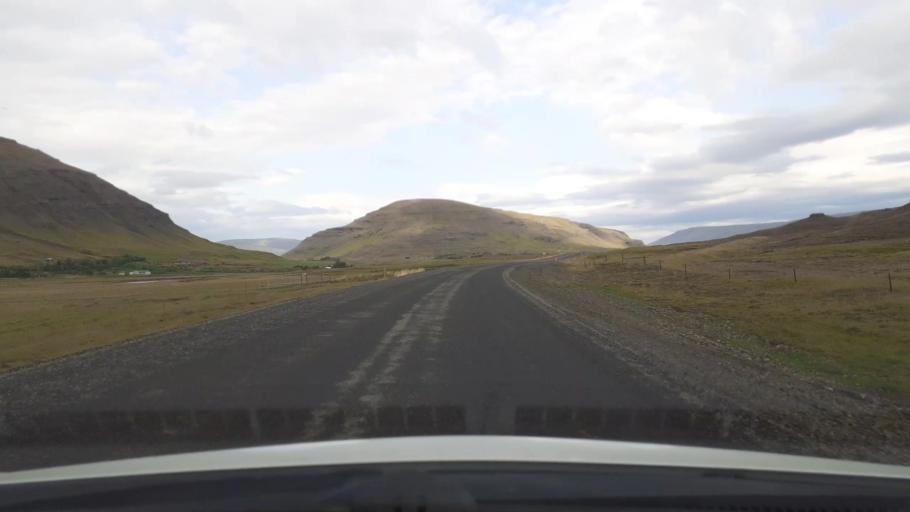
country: IS
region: Capital Region
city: Mosfellsbaer
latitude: 64.2999
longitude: -21.4801
